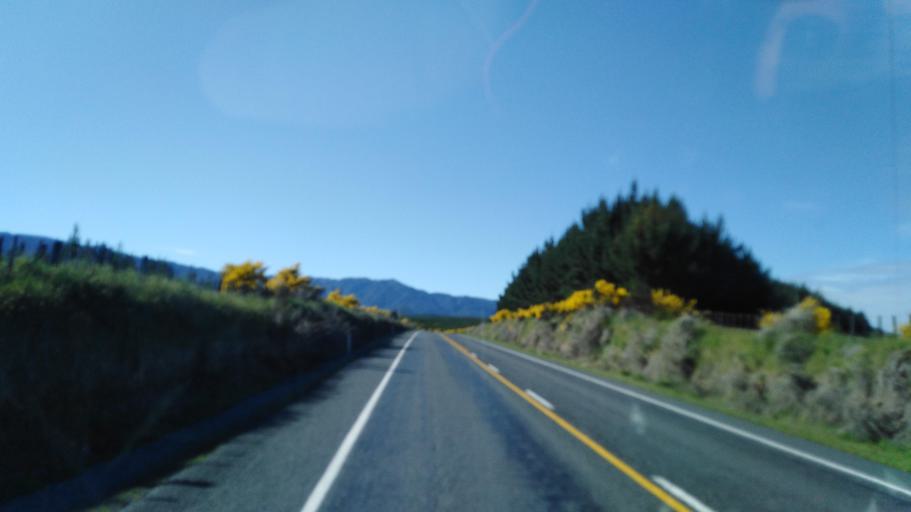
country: NZ
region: Waikato
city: Turangi
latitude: -39.0879
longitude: 175.8080
